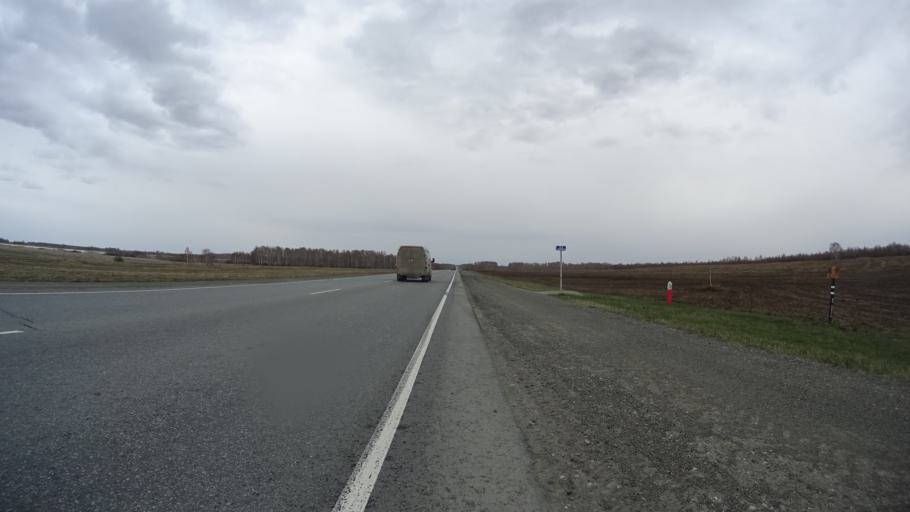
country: RU
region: Chelyabinsk
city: Krasnogorskiy
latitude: 54.6636
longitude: 61.2538
